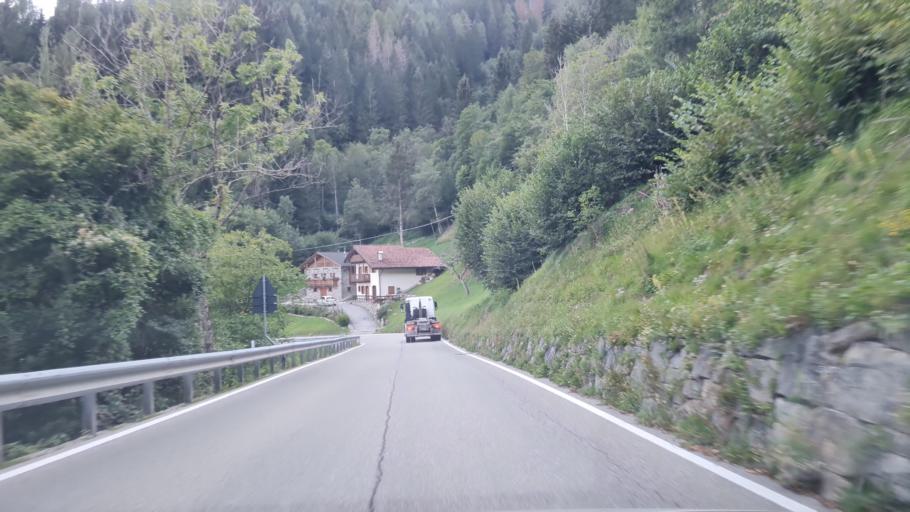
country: IT
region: Trentino-Alto Adige
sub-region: Provincia di Trento
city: Siror
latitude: 46.1943
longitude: 11.8234
